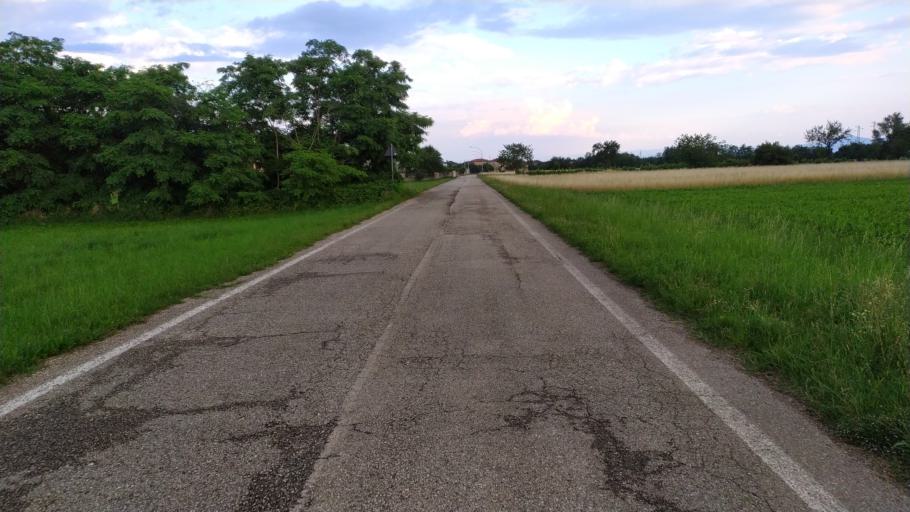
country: IT
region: Veneto
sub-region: Provincia di Vicenza
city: Carre
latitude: 45.7554
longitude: 11.4522
